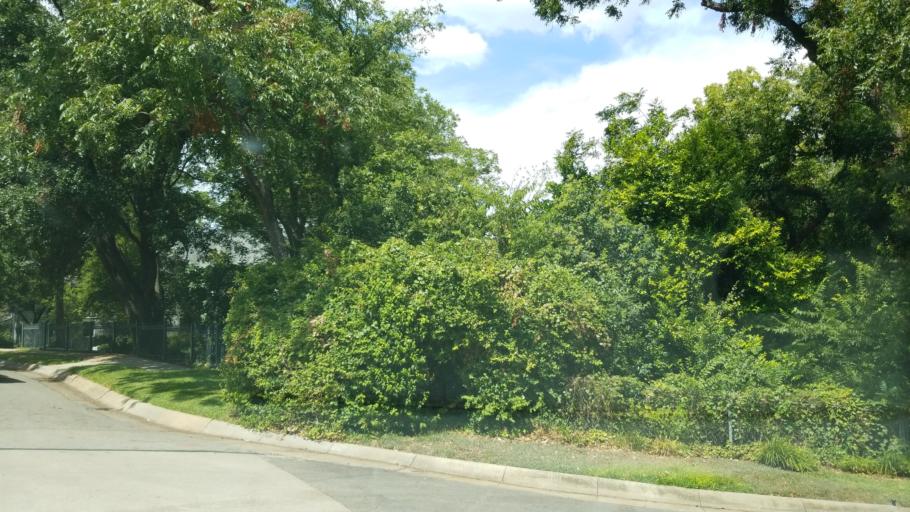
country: US
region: Texas
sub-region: Dallas County
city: Cockrell Hill
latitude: 32.7560
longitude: -96.8456
